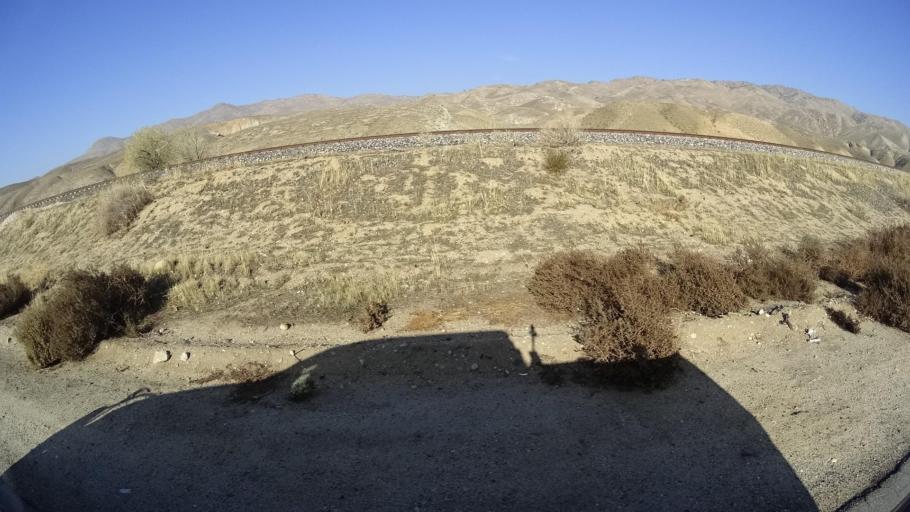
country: US
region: California
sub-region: Kern County
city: Arvin
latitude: 35.3212
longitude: -118.7114
